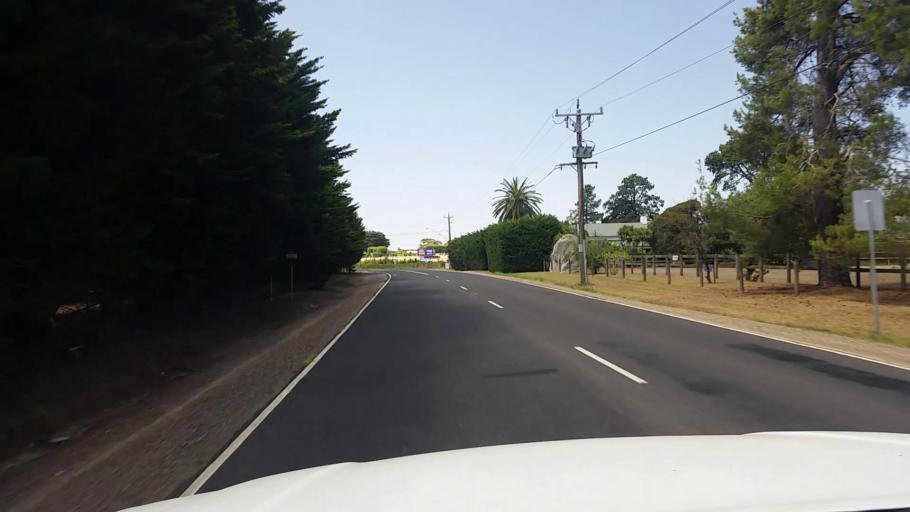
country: AU
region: Victoria
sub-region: Mornington Peninsula
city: Moorooduc
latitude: -38.2551
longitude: 145.1257
